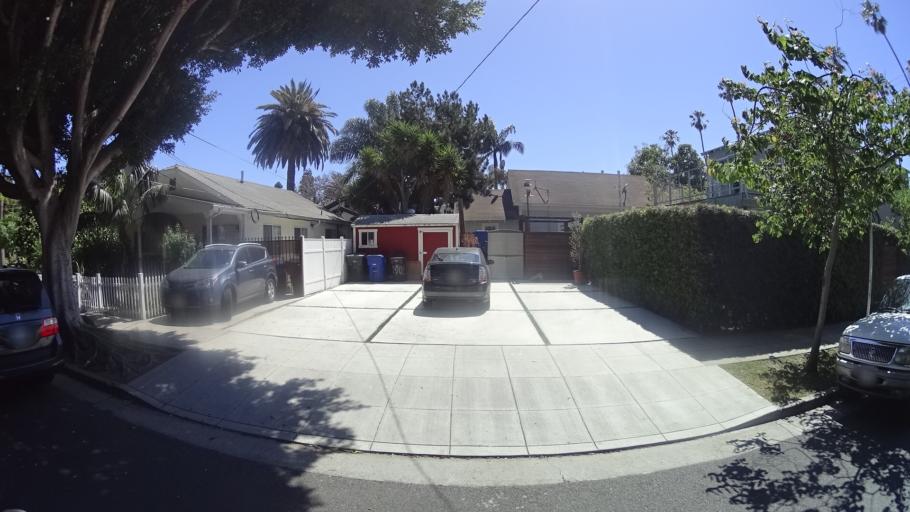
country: US
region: California
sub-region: Los Angeles County
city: Santa Monica
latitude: 34.0093
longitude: -118.4854
